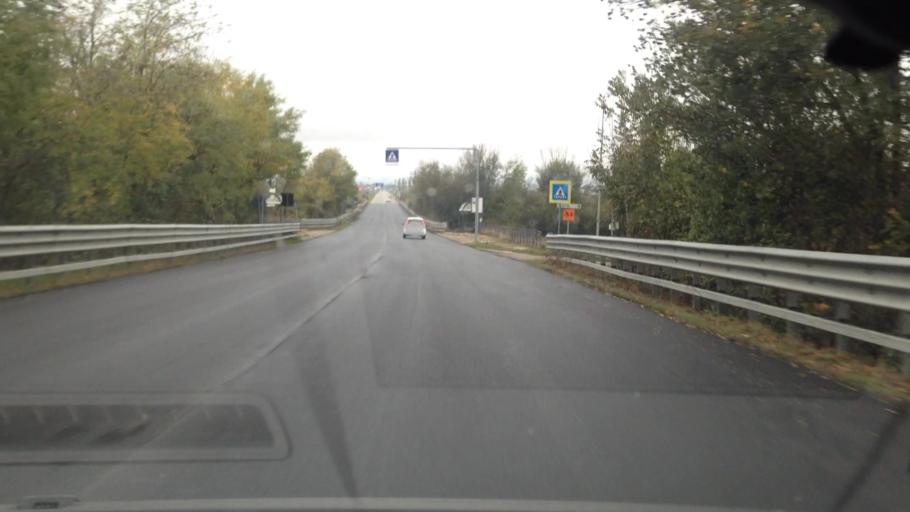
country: IT
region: Piedmont
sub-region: Provincia di Torino
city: Riva Presso Chieri
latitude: 44.9649
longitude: 7.9050
